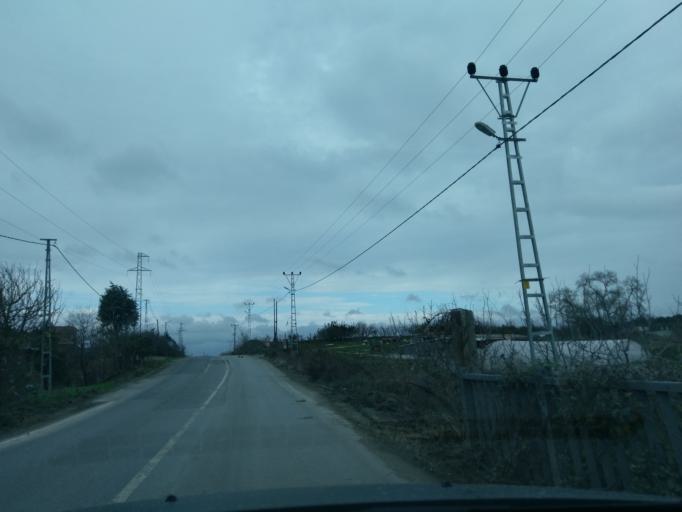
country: TR
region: Istanbul
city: Catalca
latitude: 41.1952
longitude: 28.3956
